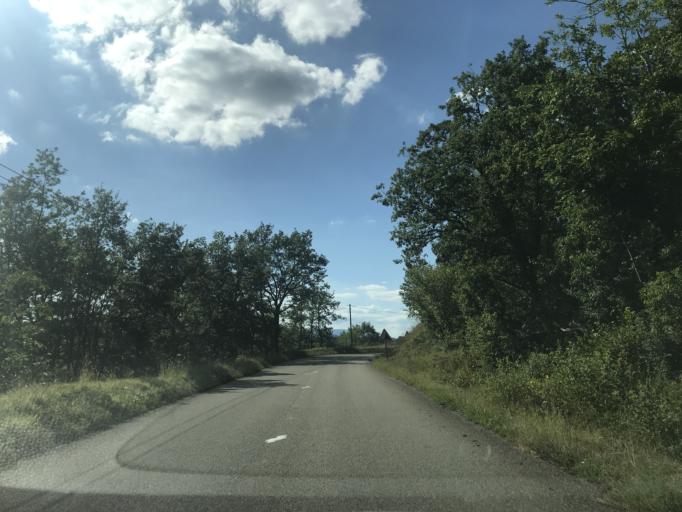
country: FR
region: Rhone-Alpes
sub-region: Departement de la Savoie
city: Brison-Saint-Innocent
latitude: 45.7037
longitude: 5.8303
